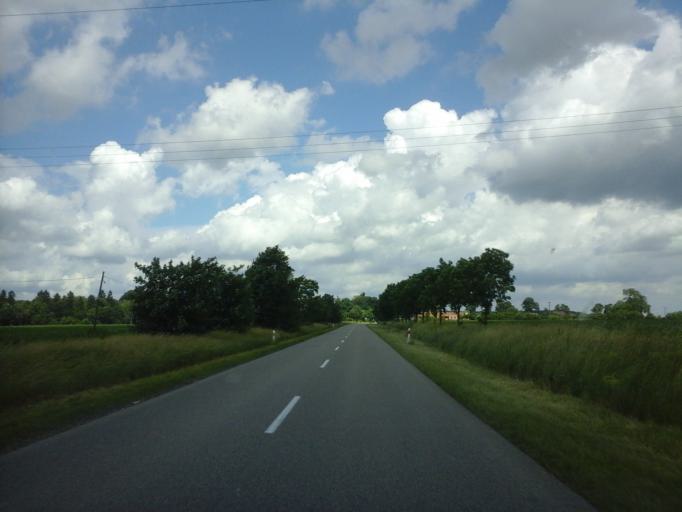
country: PL
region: West Pomeranian Voivodeship
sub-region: Powiat swidwinski
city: Slawoborze
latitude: 53.9489
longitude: 15.6711
